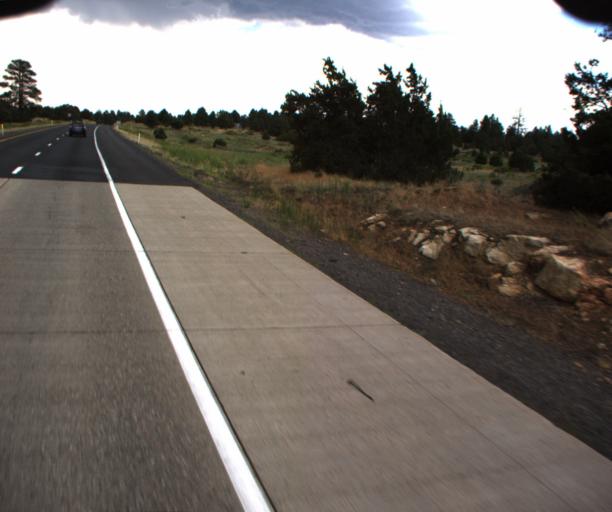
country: US
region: Arizona
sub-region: Coconino County
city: Flagstaff
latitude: 35.2179
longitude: -111.5609
